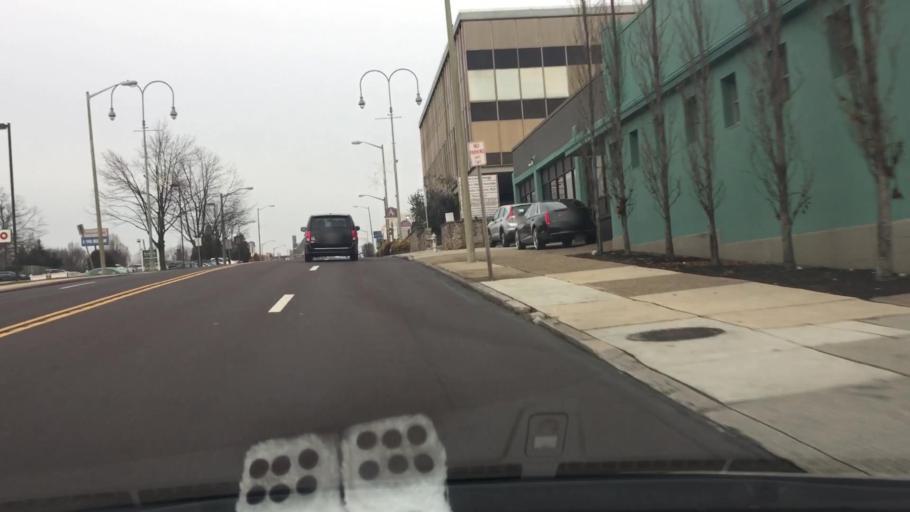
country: US
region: Pennsylvania
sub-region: Montgomery County
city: Ardmore
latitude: 40.0037
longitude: -75.2825
